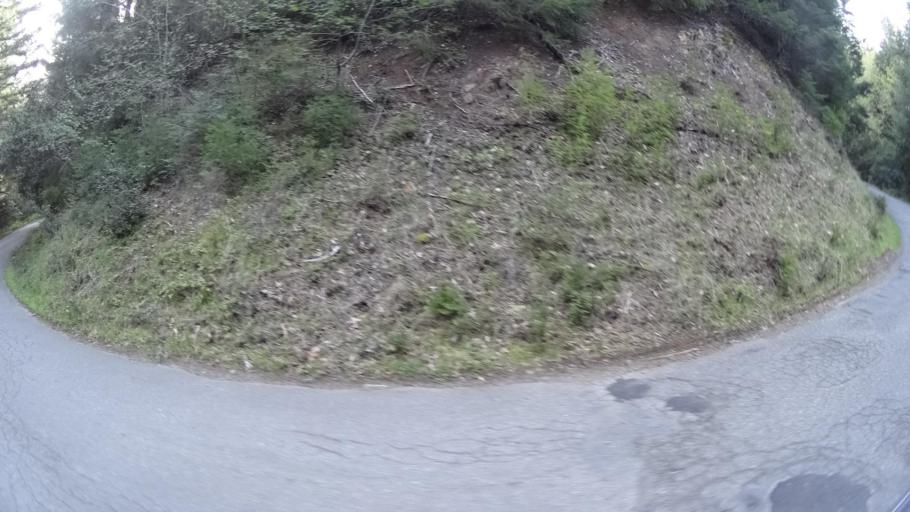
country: US
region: California
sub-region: Humboldt County
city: Bayside
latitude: 40.6953
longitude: -123.9422
